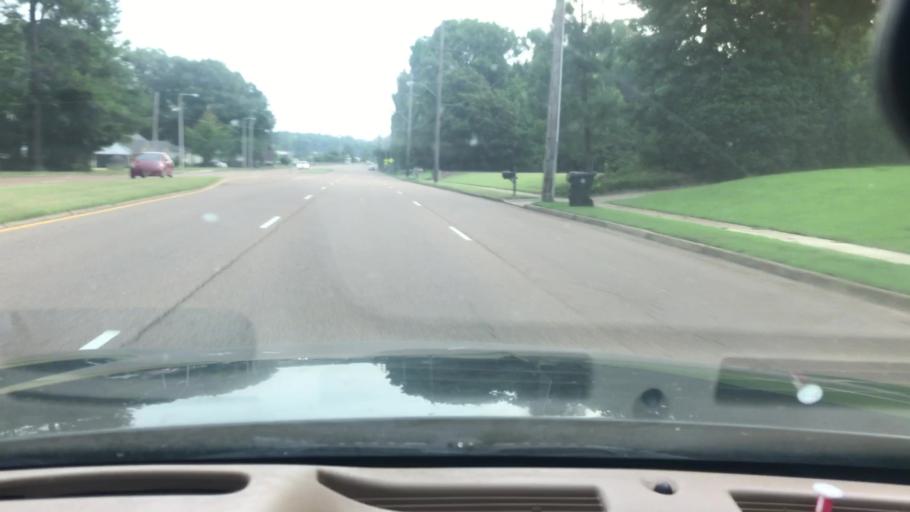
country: US
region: Tennessee
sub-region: Shelby County
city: Bartlett
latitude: 35.1946
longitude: -89.8691
